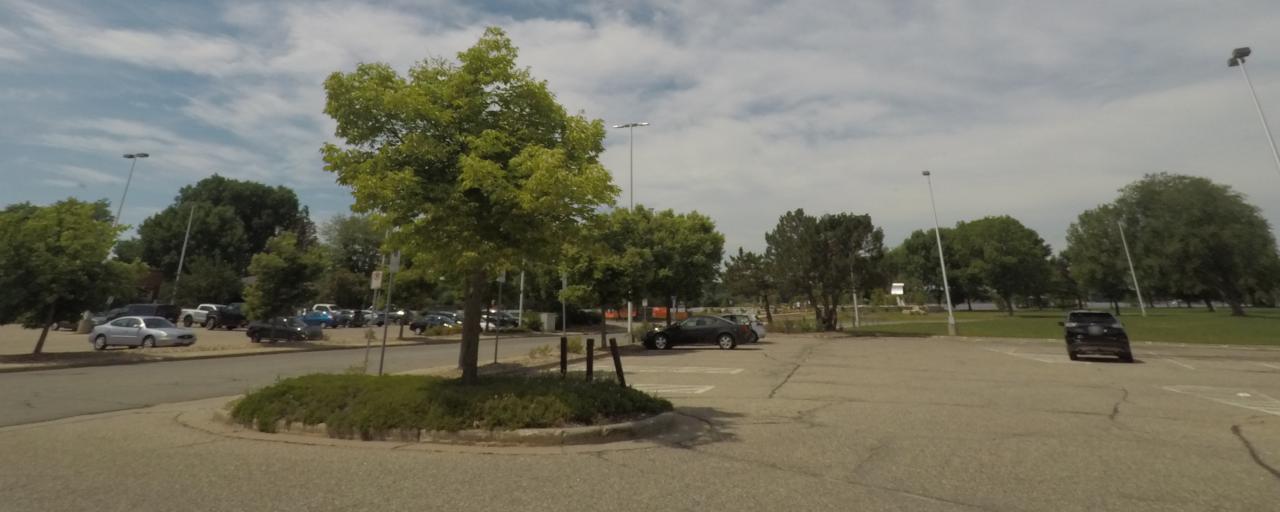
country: US
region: Wisconsin
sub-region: Portage County
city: Stevens Point
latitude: 44.5244
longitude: -89.5876
